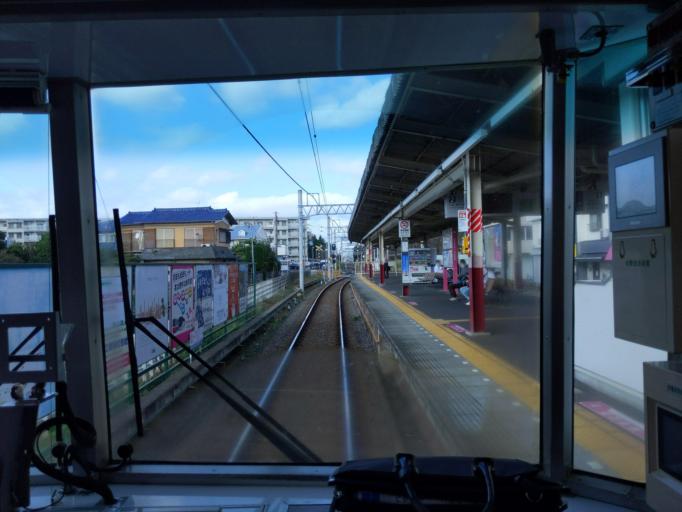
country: JP
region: Chiba
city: Kashiwa
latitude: 35.7825
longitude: 139.9757
